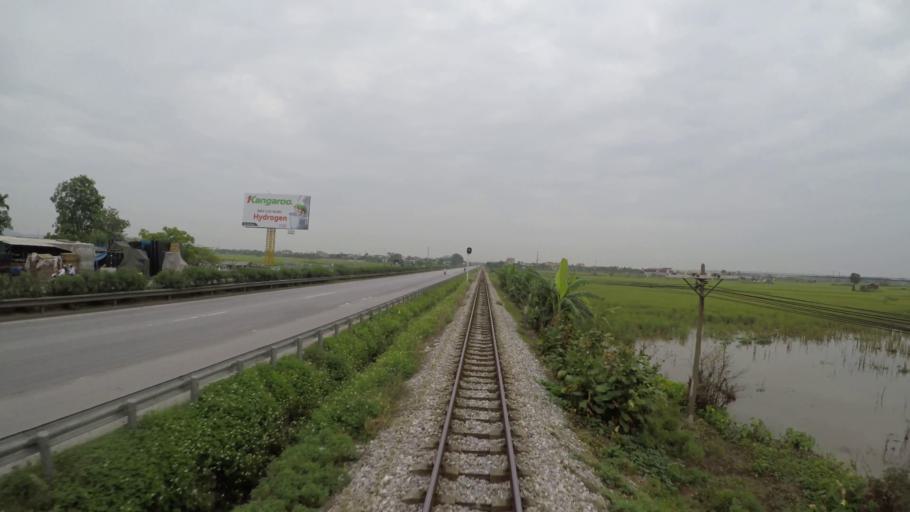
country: VN
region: Hai Duong
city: Thanh Ha
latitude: 20.9772
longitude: 106.4294
